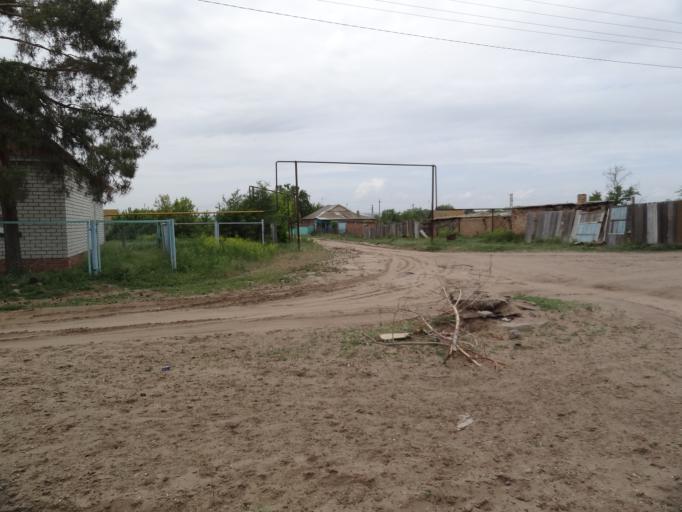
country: RU
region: Saratov
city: Privolzhskiy
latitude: 51.1812
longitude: 45.9174
